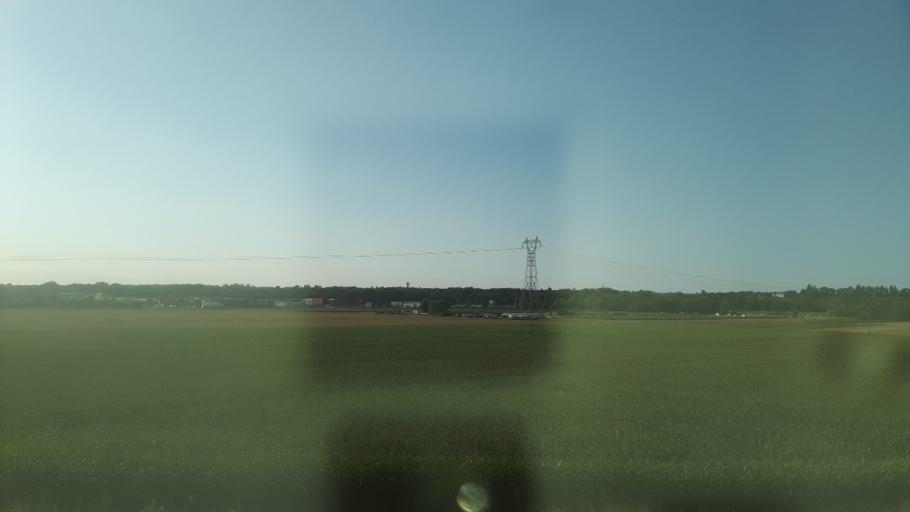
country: FR
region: Centre
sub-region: Departement d'Indre-et-Loire
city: Vouvray
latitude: 47.3940
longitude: 0.7965
